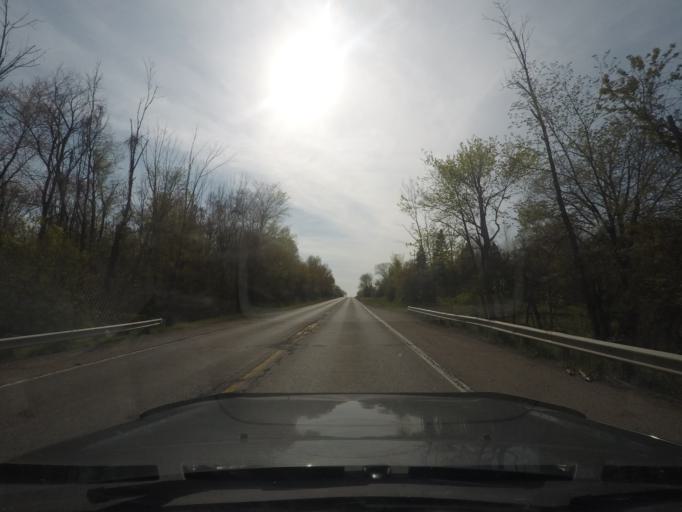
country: US
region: Michigan
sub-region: Berrien County
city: Buchanan
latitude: 41.7932
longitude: -86.4367
